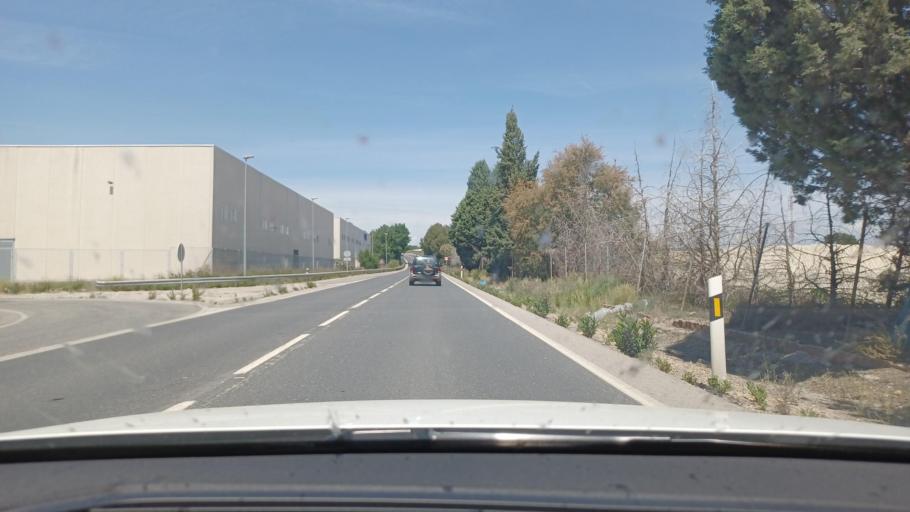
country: ES
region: Madrid
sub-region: Provincia de Madrid
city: Meco
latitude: 40.5340
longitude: -3.2930
